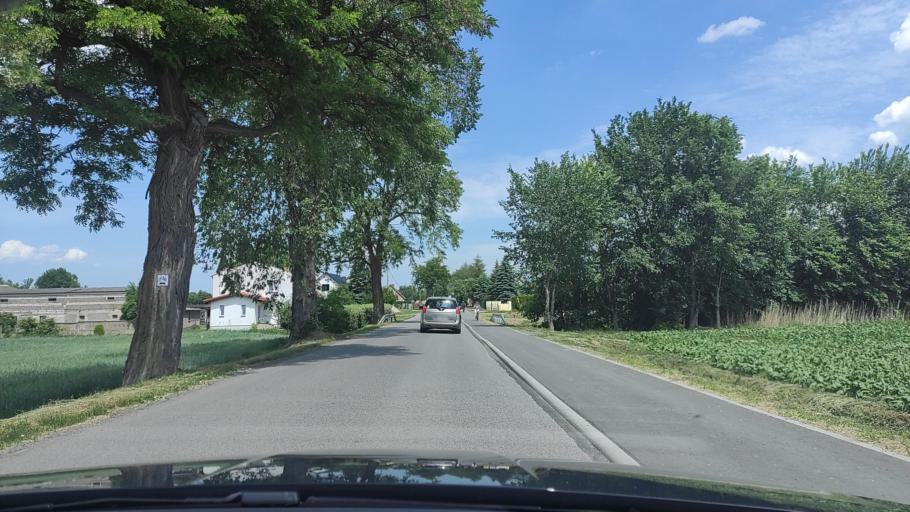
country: PL
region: Greater Poland Voivodeship
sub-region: Powiat gnieznienski
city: Lubowo
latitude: 52.5157
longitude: 17.3858
